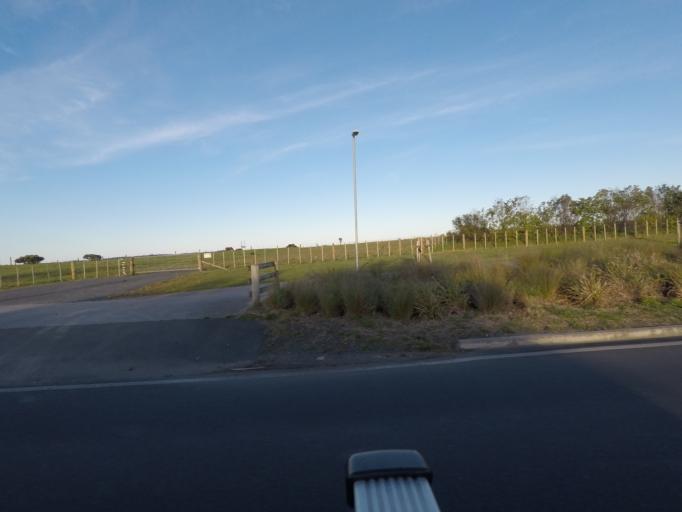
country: NZ
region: Auckland
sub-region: Auckland
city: Rosebank
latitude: -36.8549
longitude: 174.6515
